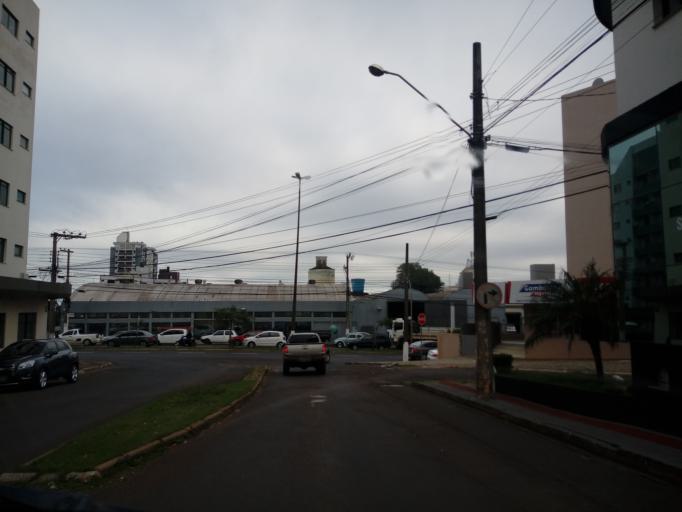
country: BR
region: Santa Catarina
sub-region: Chapeco
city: Chapeco
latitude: -27.0912
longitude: -52.6155
